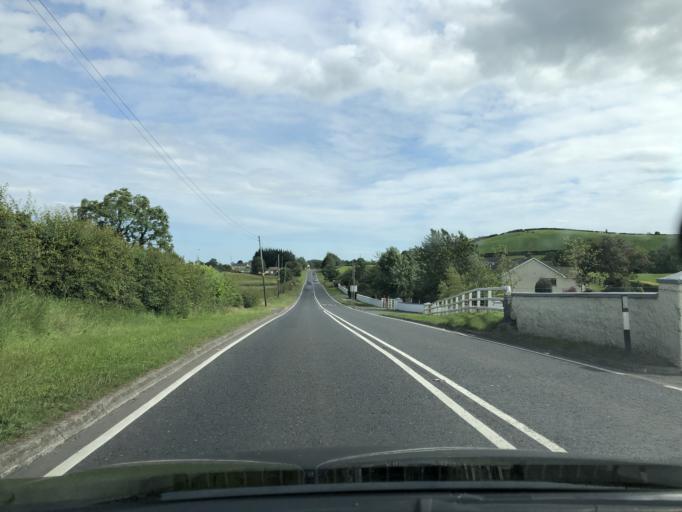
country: GB
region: Northern Ireland
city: Ballynahinch
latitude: 54.3830
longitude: -5.8775
